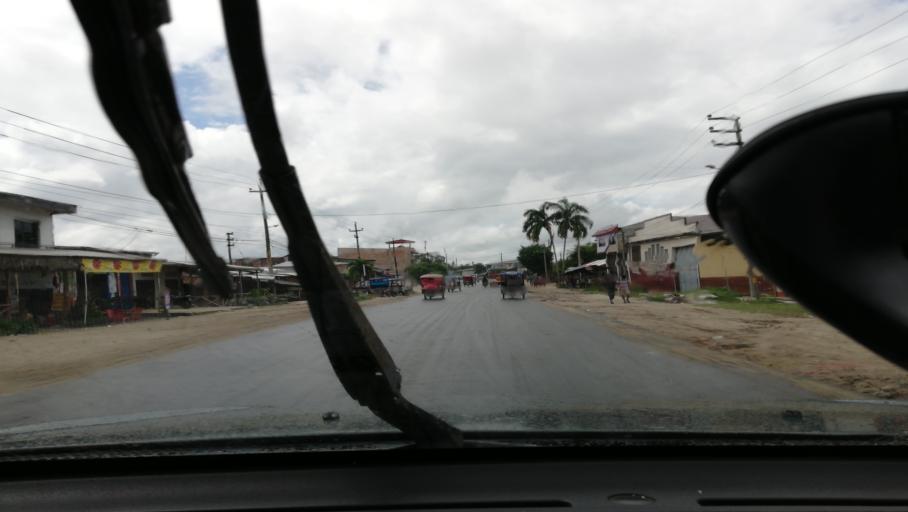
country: PE
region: Loreto
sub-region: Provincia de Maynas
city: Iquitos
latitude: -3.7962
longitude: -73.3018
